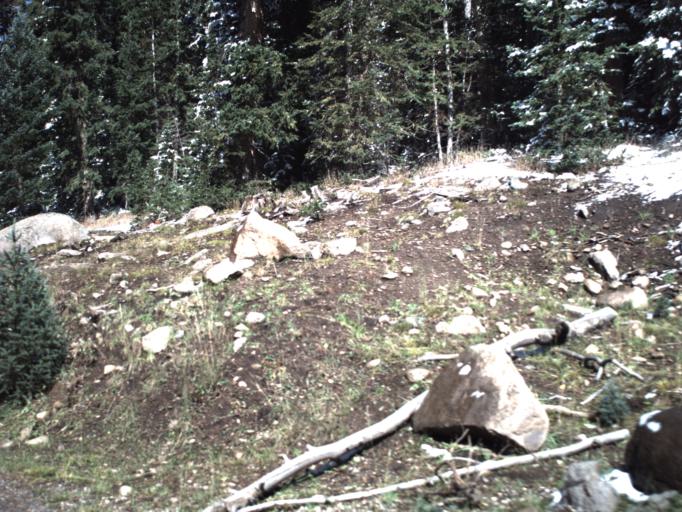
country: US
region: Utah
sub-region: Piute County
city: Junction
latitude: 38.2884
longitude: -112.3579
